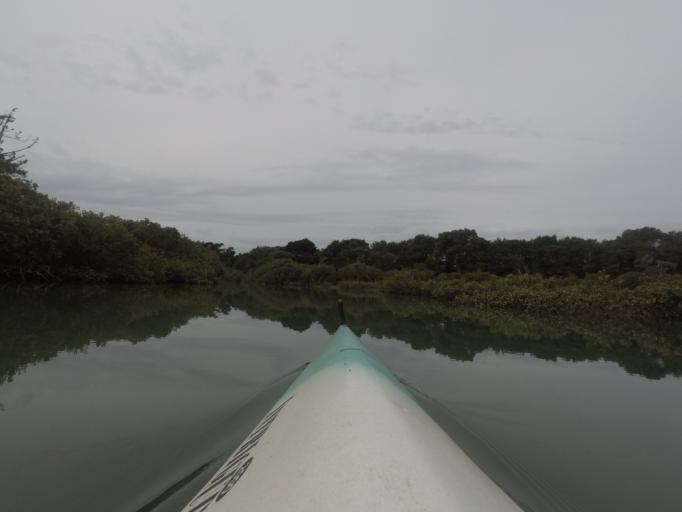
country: NZ
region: Auckland
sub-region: Auckland
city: Rothesay Bay
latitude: -36.6790
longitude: 174.7076
